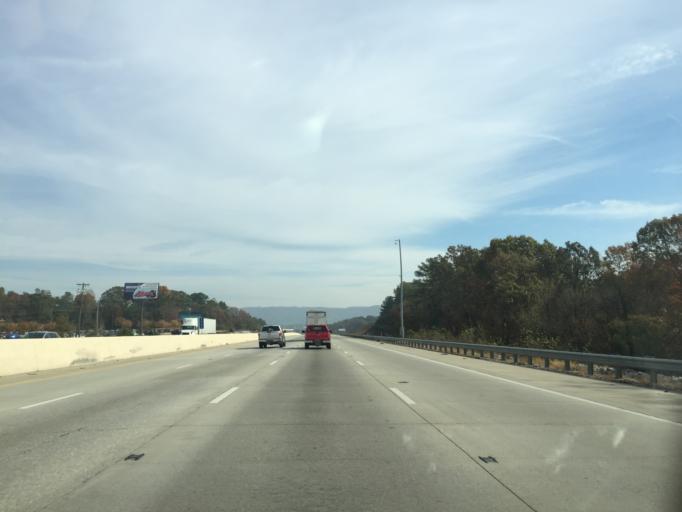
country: US
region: Tennessee
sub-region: Hamilton County
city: Collegedale
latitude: 35.0810
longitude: -85.0849
